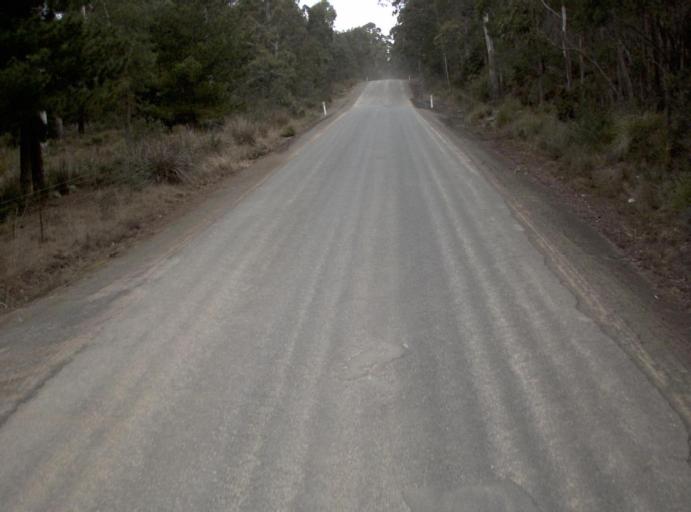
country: AU
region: Tasmania
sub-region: Launceston
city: Mayfield
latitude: -41.3487
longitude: 147.2175
